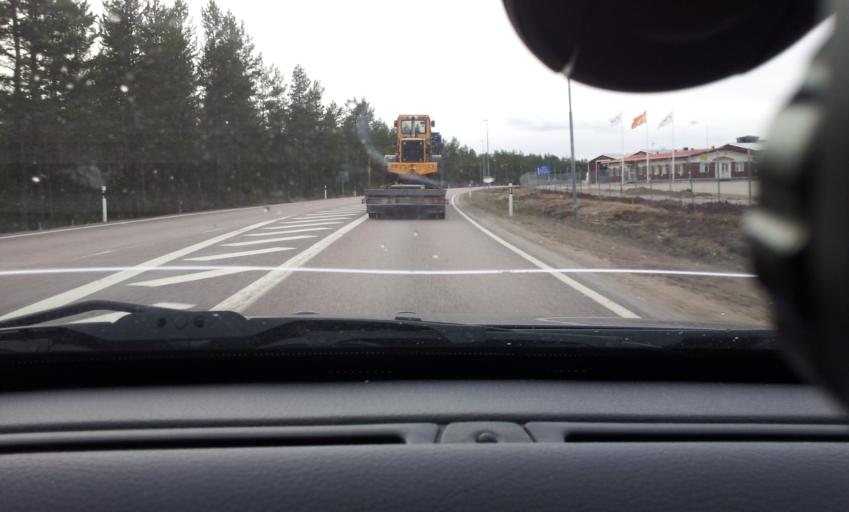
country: SE
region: Gaevleborg
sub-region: Ljusdals Kommun
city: Farila
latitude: 61.8036
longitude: 15.7848
